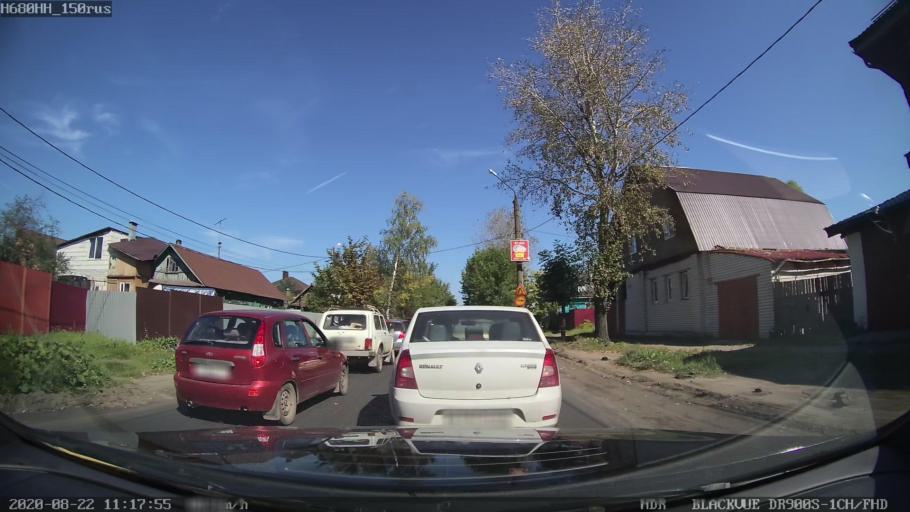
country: RU
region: Tverskaya
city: Tver
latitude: 56.8755
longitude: 35.9289
